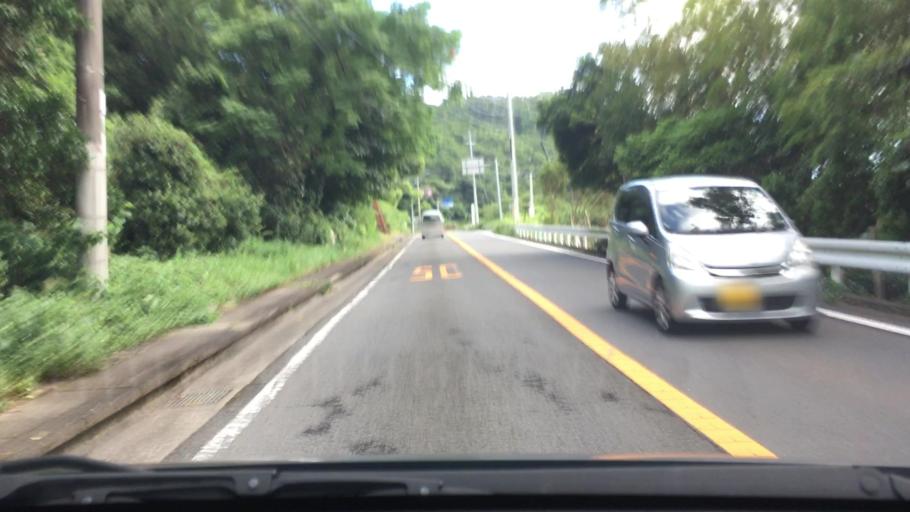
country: JP
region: Nagasaki
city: Togitsu
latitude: 32.8267
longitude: 129.7254
